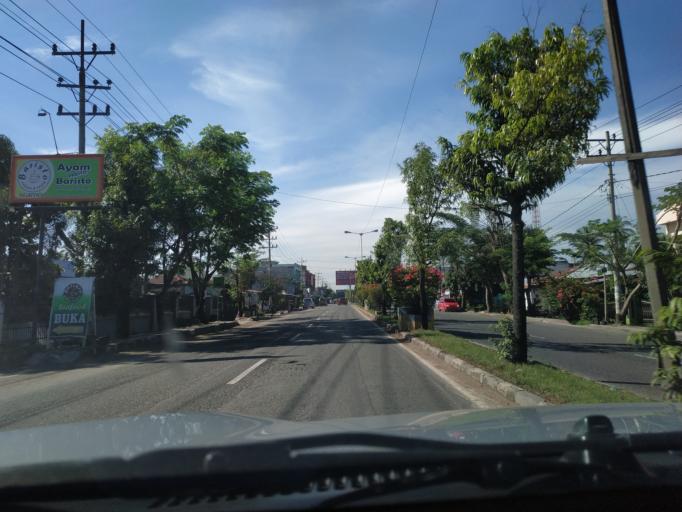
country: ID
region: North Sumatra
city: Tebingtinggi
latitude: 3.3616
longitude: 99.1669
